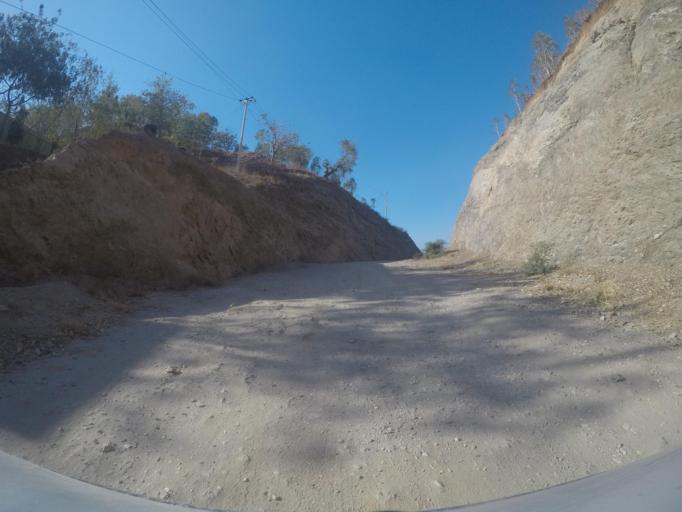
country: TL
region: Dili
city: Dili
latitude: -8.5304
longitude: 125.6202
